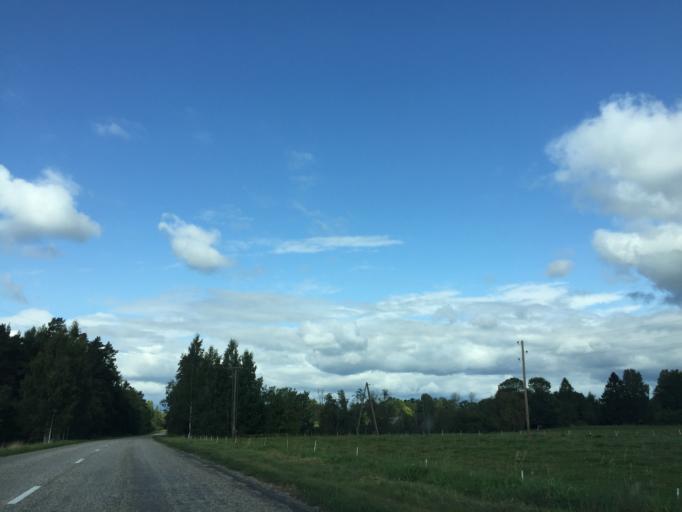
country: LV
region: Pargaujas
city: Stalbe
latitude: 57.4019
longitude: 24.9766
